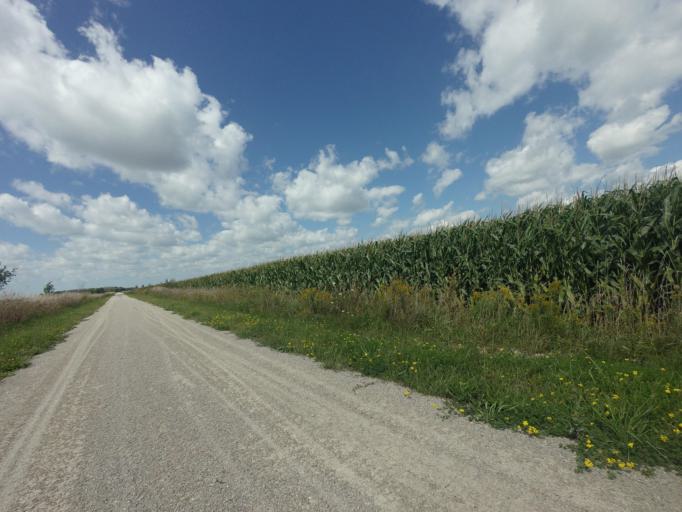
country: CA
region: Ontario
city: Huron East
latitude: 43.6066
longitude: -81.1213
